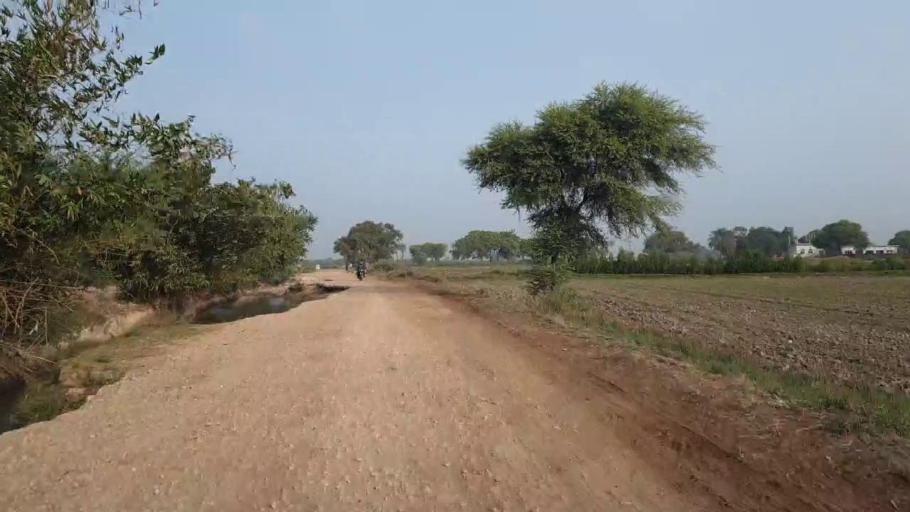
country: PK
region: Sindh
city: Tando Muhammad Khan
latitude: 25.1397
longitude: 68.5923
